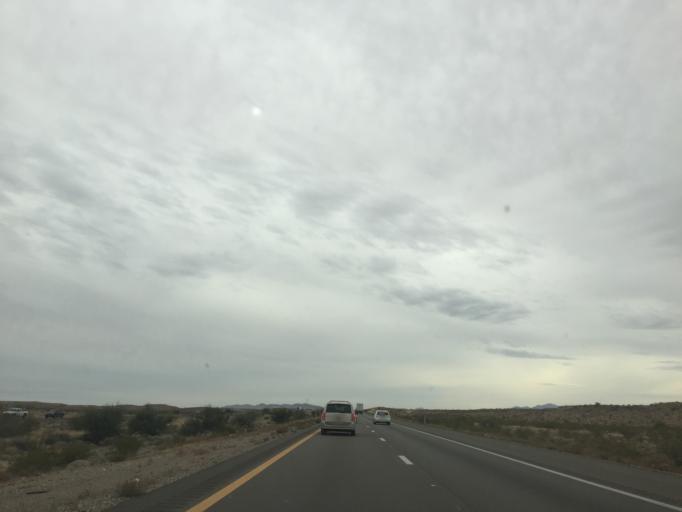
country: US
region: Nevada
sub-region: Clark County
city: Moapa Town
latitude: 36.5417
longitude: -114.7121
